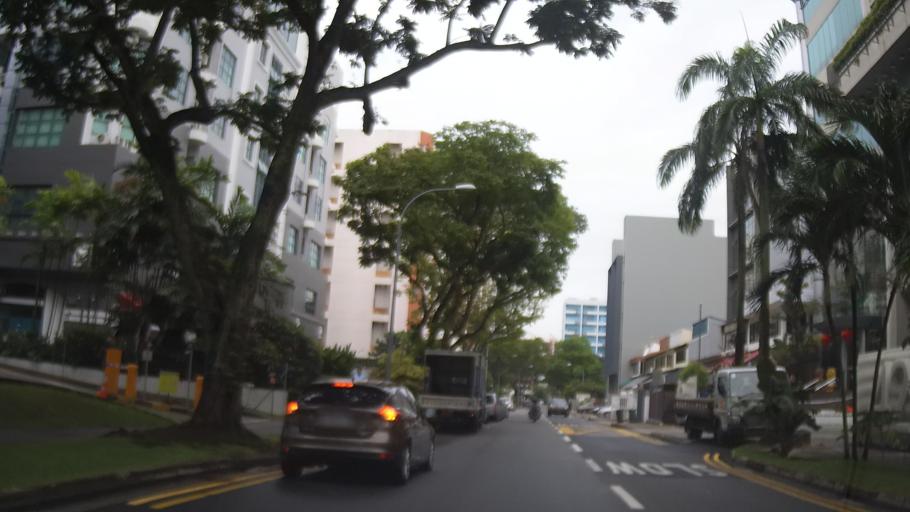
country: SG
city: Singapore
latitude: 1.3284
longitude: 103.8765
